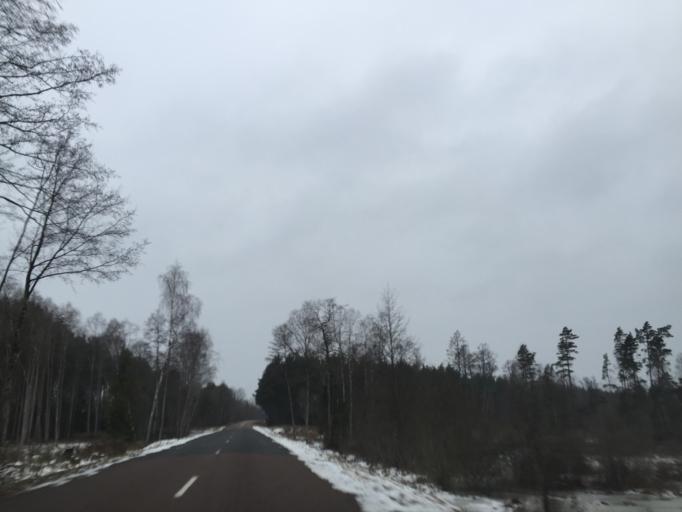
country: EE
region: Saare
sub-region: Kuressaare linn
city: Kuressaare
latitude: 58.3870
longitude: 22.2263
